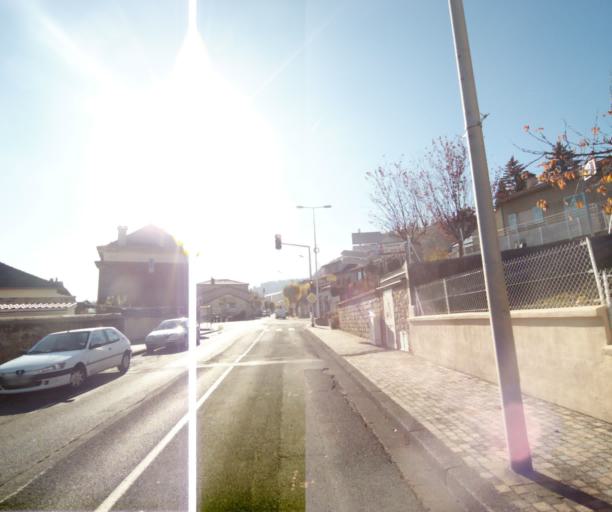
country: FR
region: Auvergne
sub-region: Departement du Puy-de-Dome
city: Ceyrat
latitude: 45.7343
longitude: 3.0641
